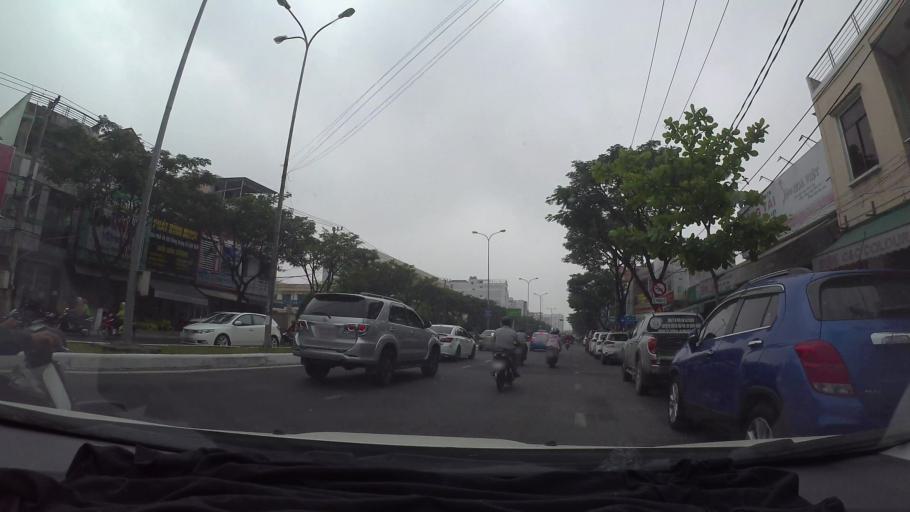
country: VN
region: Da Nang
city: Da Nang
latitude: 16.0452
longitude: 108.2098
